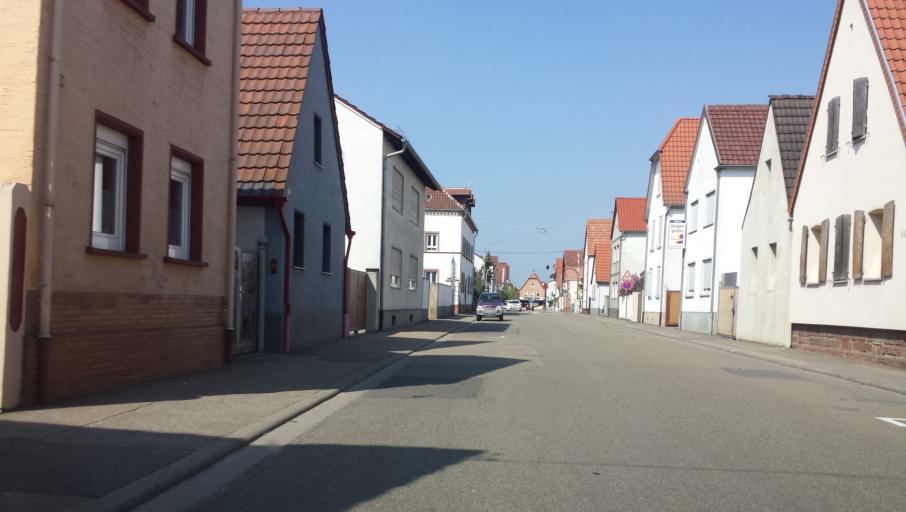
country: DE
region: Rheinland-Pfalz
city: Lingenfeld
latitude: 49.2470
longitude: 8.3434
